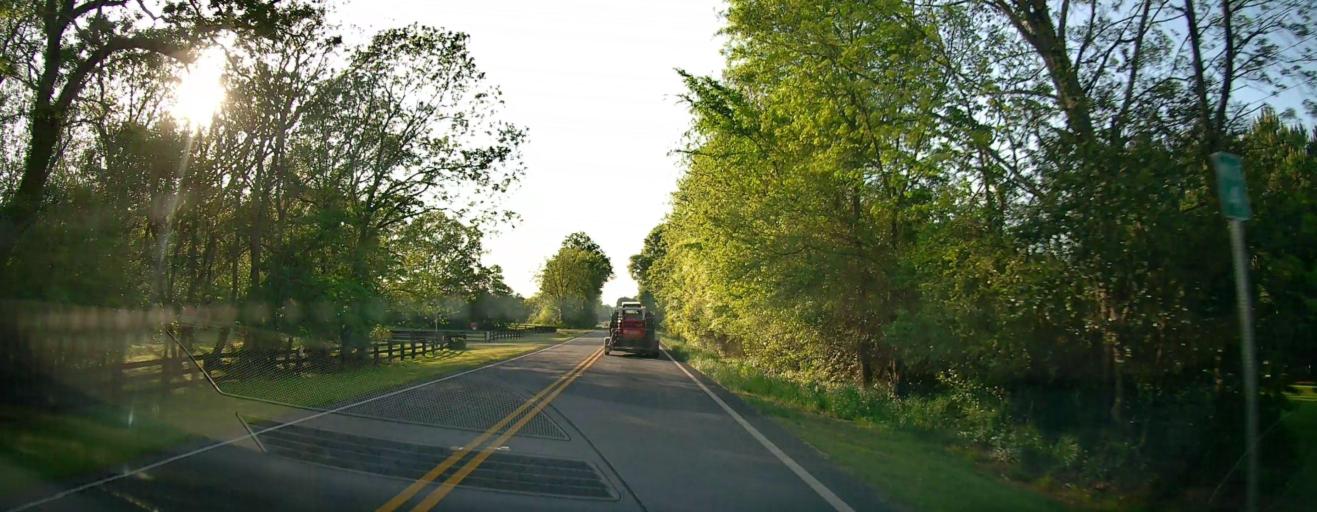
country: US
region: Georgia
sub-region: Jasper County
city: Monticello
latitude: 33.4039
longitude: -83.5946
